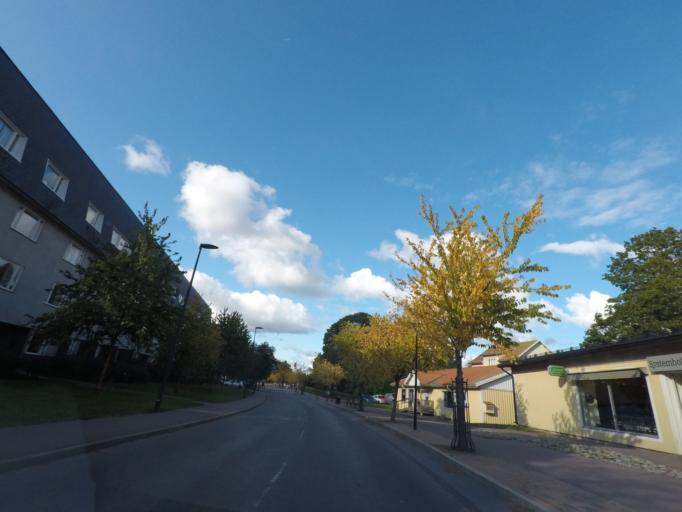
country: SE
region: Vaestmanland
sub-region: Skinnskattebergs Kommun
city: Skinnskatteberg
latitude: 59.8306
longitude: 15.6934
